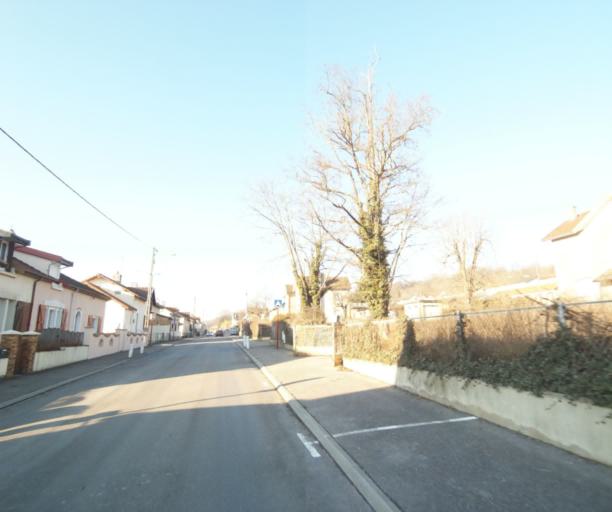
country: FR
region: Champagne-Ardenne
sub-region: Departement de la Haute-Marne
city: Bienville
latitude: 48.5545
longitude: 5.0759
